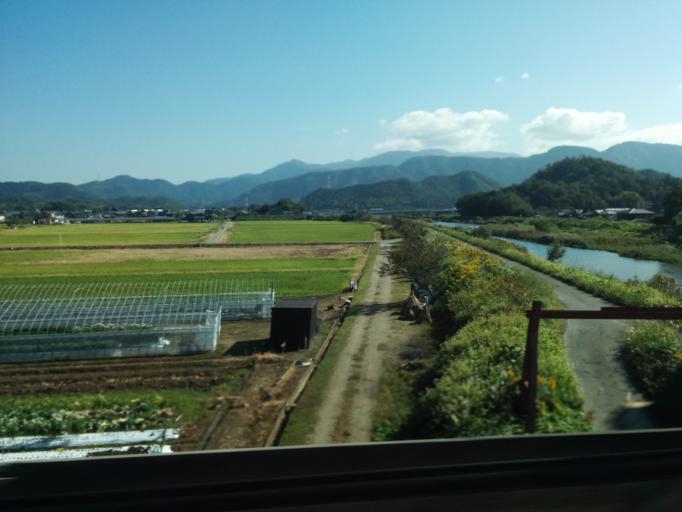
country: JP
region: Shiga Prefecture
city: Nagahama
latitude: 35.3341
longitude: 136.2948
